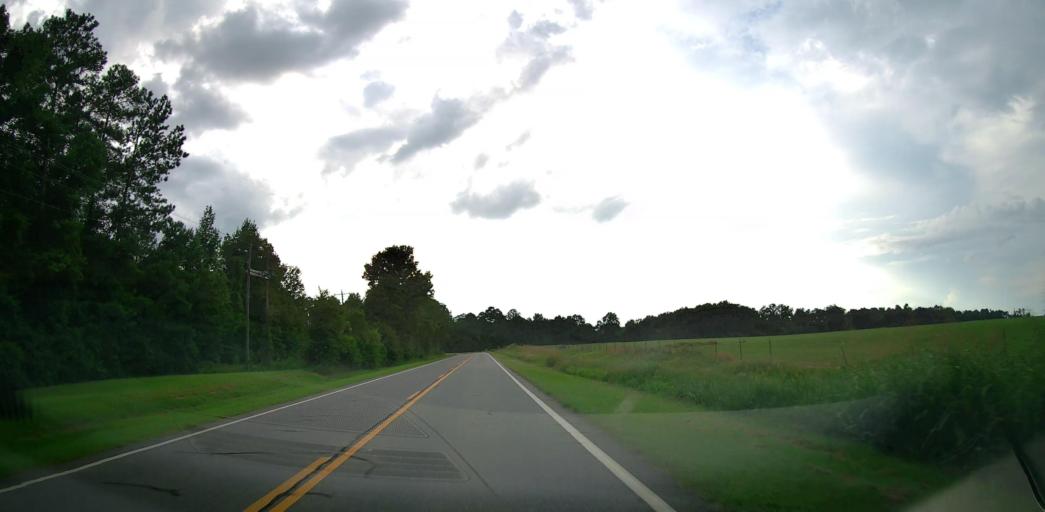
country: US
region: Georgia
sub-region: Pulaski County
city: Hawkinsville
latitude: 32.2946
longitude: -83.5198
